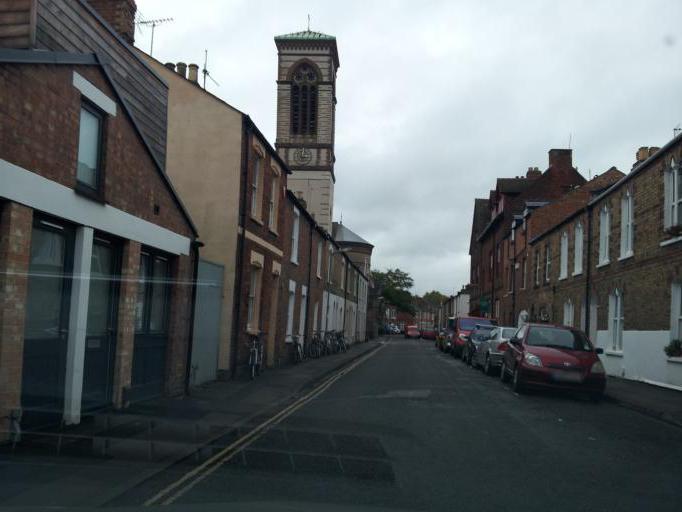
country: GB
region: England
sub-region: Oxfordshire
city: Oxford
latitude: 51.7575
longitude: -1.2688
